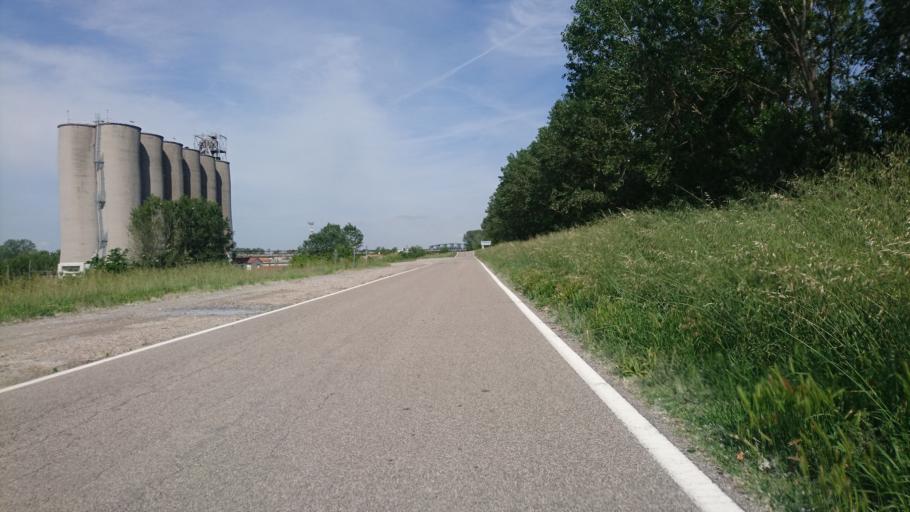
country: IT
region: Lombardy
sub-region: Provincia di Mantova
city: Revere
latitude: 45.0469
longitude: 11.1435
